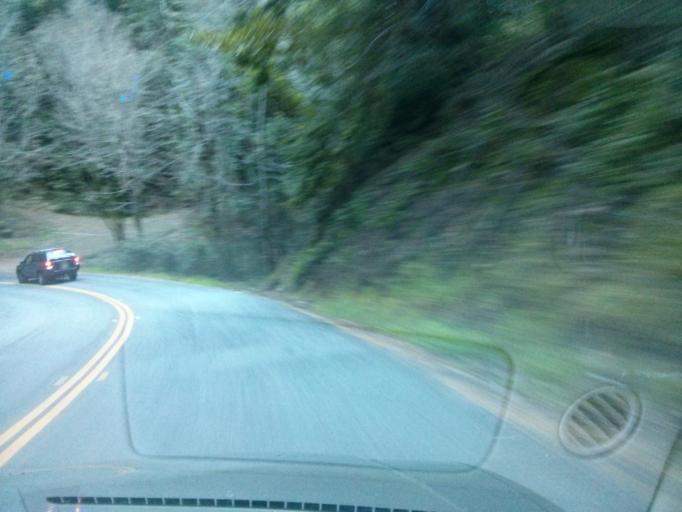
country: US
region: California
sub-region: Santa Cruz County
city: Felton
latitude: 37.0520
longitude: -122.0952
